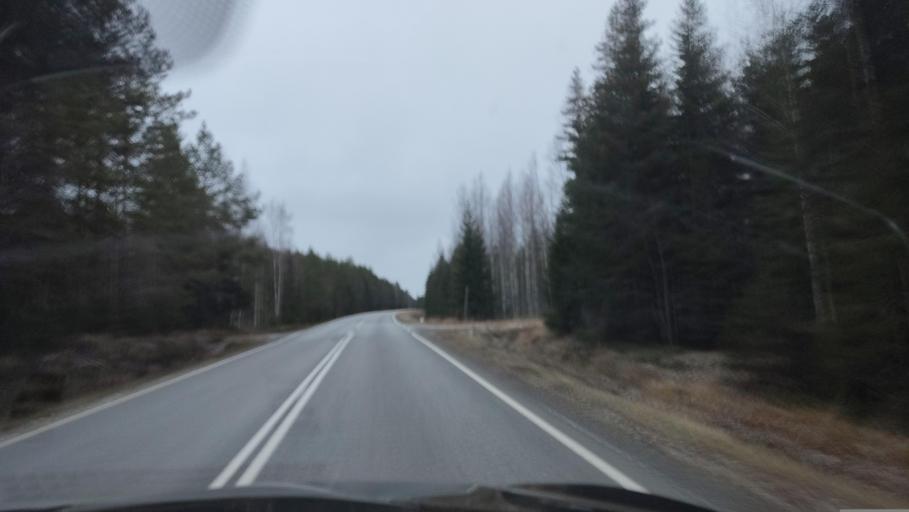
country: FI
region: Southern Ostrobothnia
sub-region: Suupohja
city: Isojoki
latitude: 62.3377
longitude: 21.9344
